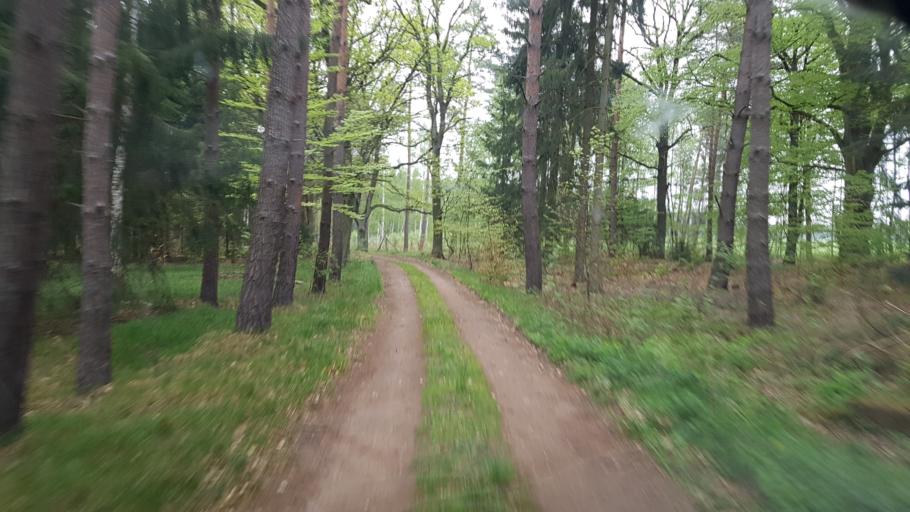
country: DE
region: Brandenburg
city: Schonewalde
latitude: 51.7084
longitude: 13.5273
